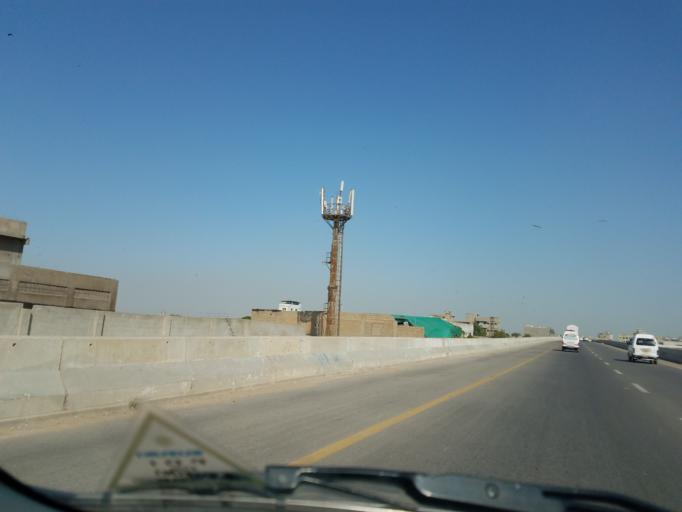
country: PK
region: Sindh
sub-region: Karachi District
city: Karachi
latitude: 24.8822
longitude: 67.0012
